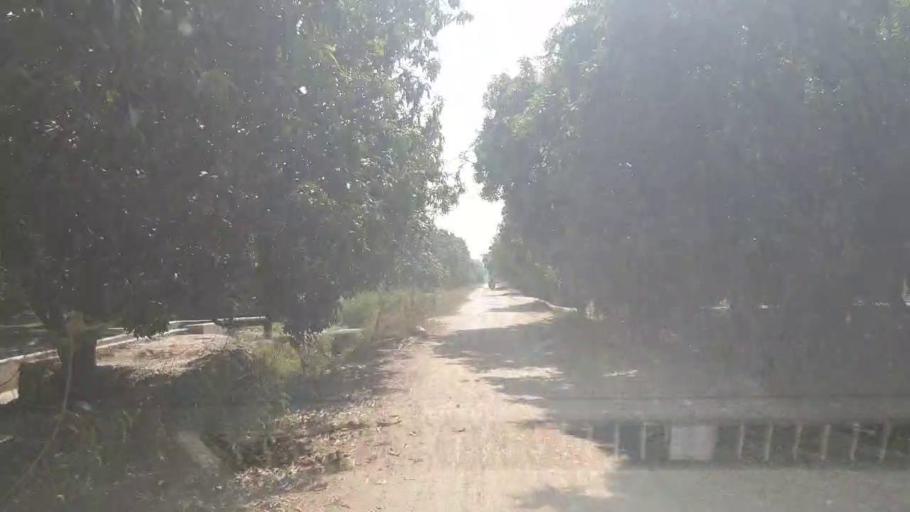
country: PK
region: Sindh
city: Tando Allahyar
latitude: 25.4718
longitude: 68.8500
